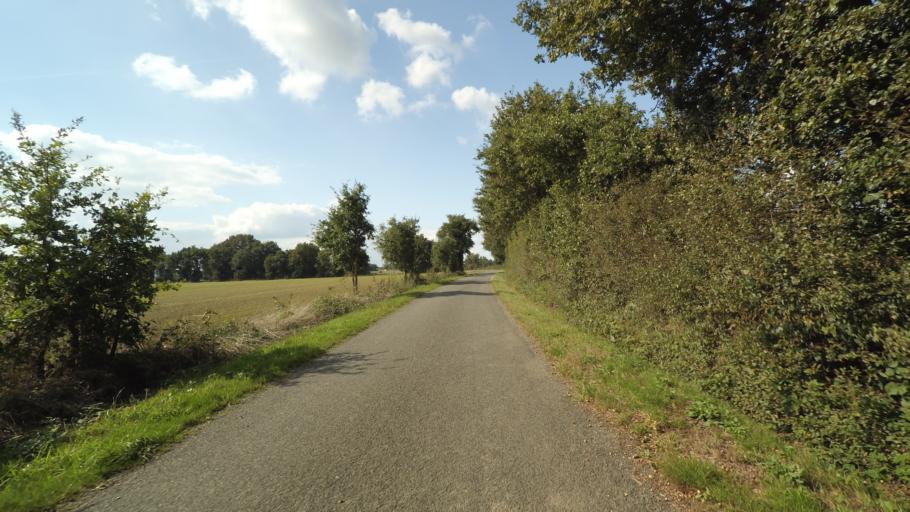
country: FR
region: Pays de la Loire
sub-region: Departement de la Vendee
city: Saint-Andre-Treize-Voies
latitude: 46.9682
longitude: -1.3851
